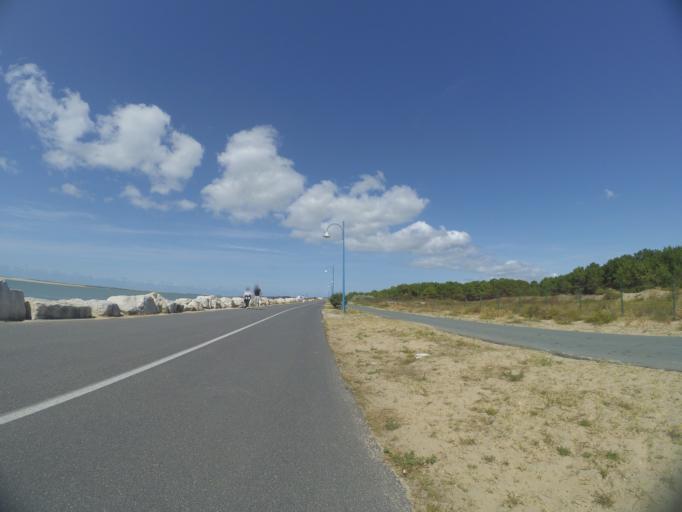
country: FR
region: Poitou-Charentes
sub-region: Departement de la Charente-Maritime
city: Les Mathes
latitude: 45.6787
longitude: -1.1735
